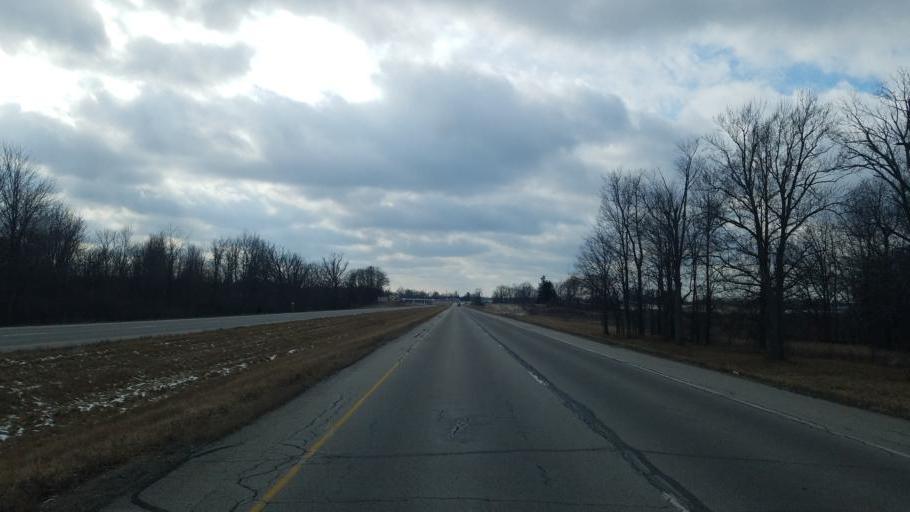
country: US
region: Ohio
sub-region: Richland County
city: Ontario
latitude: 40.7650
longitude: -82.6000
